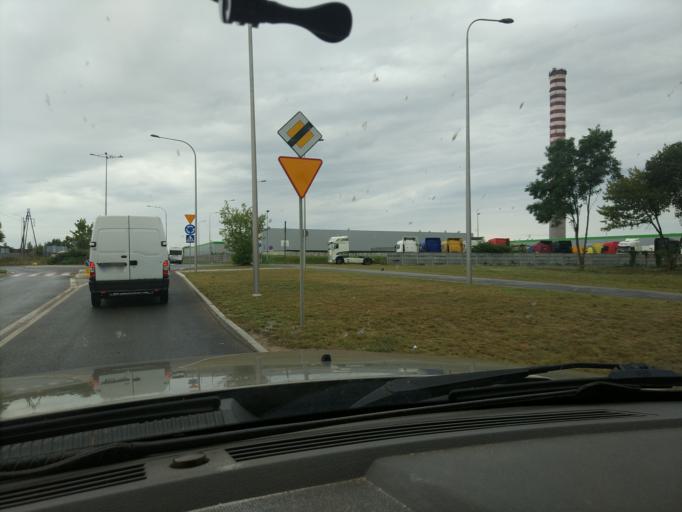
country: PL
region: Masovian Voivodeship
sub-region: Powiat pruszkowski
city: Brwinow
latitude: 52.1800
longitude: 20.7501
